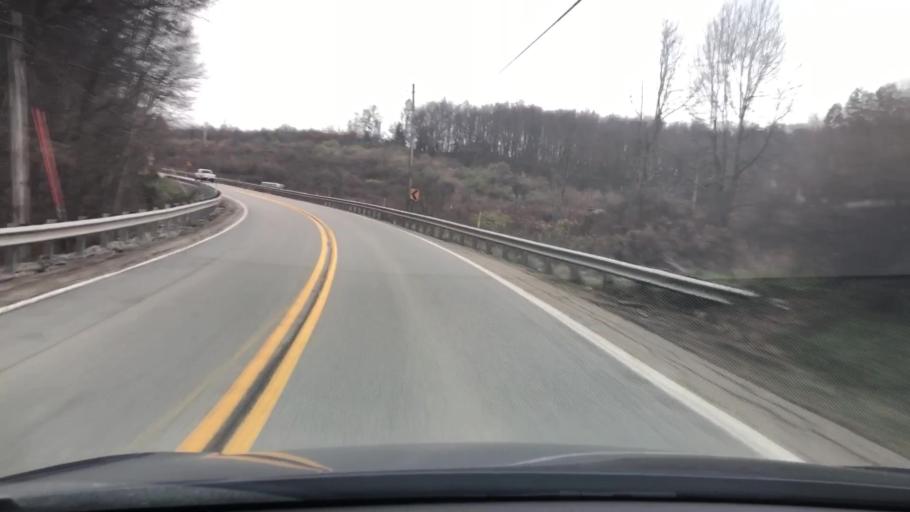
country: US
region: Pennsylvania
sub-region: Armstrong County
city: Kittanning
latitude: 40.8447
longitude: -79.4634
